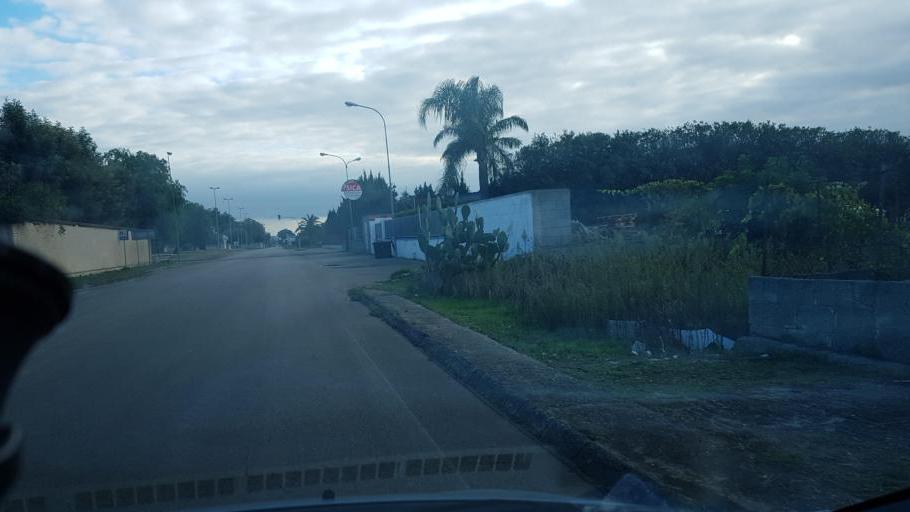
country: IT
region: Apulia
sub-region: Provincia di Lecce
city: Veglie
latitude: 40.3471
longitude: 17.9688
